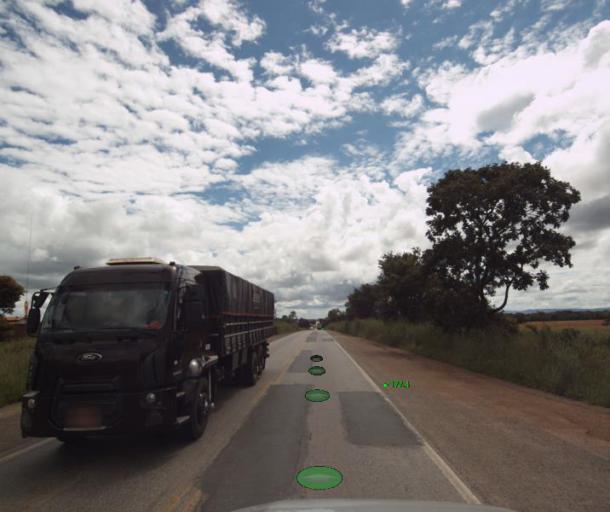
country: BR
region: Goias
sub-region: Uruacu
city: Uruacu
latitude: -14.3262
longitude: -49.1526
